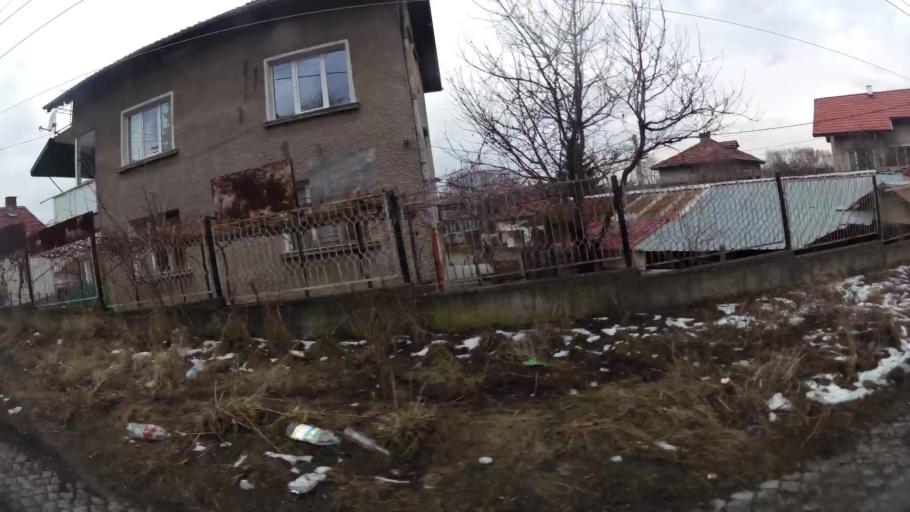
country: BG
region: Sofiya
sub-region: Obshtina Bozhurishte
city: Bozhurishte
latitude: 42.6981
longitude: 23.2272
